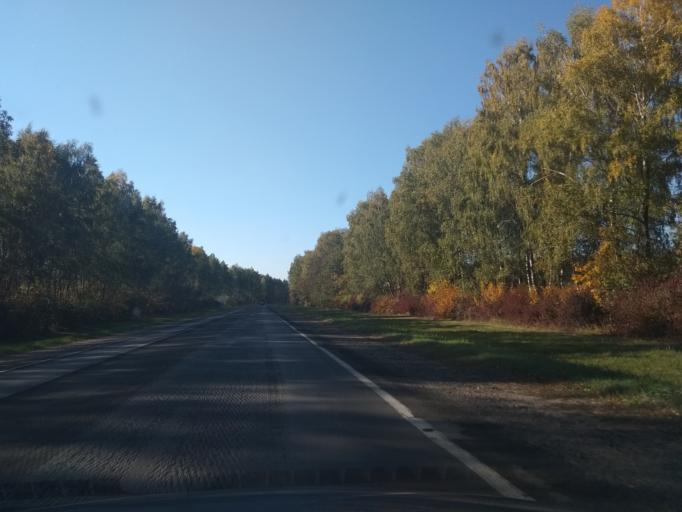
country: BY
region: Grodnenskaya
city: Zhyrovichy
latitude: 53.0590
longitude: 25.4389
